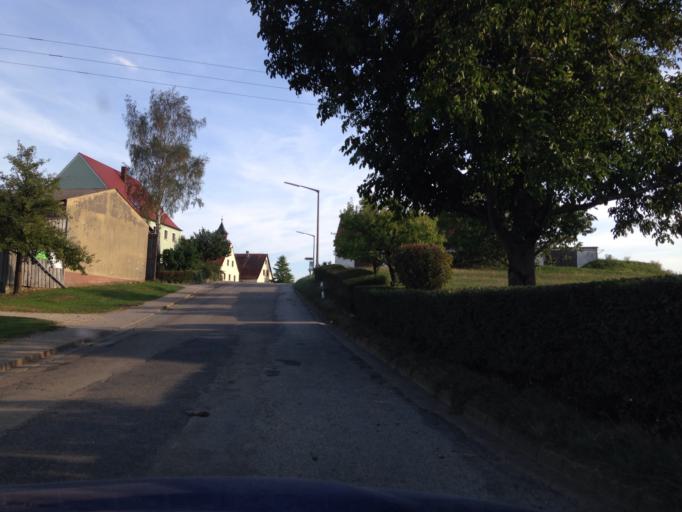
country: DE
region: Bavaria
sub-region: Regierungsbezirk Mittelfranken
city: Thalmassing
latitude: 49.1072
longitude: 11.2159
